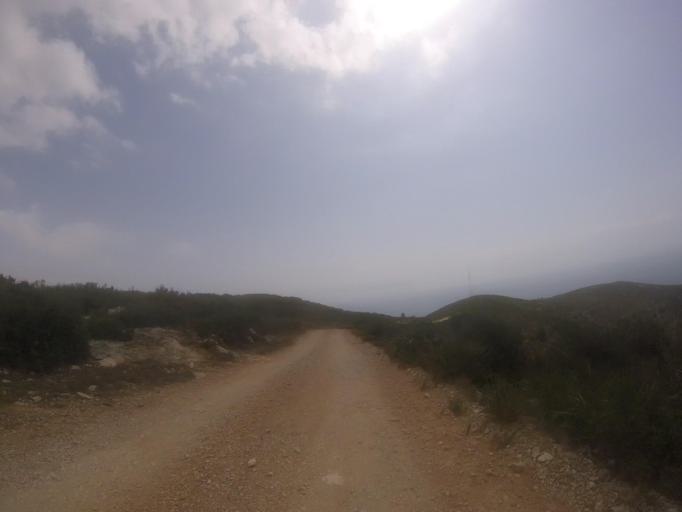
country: ES
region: Valencia
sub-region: Provincia de Castello
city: Peniscola
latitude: 40.3466
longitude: 0.3618
